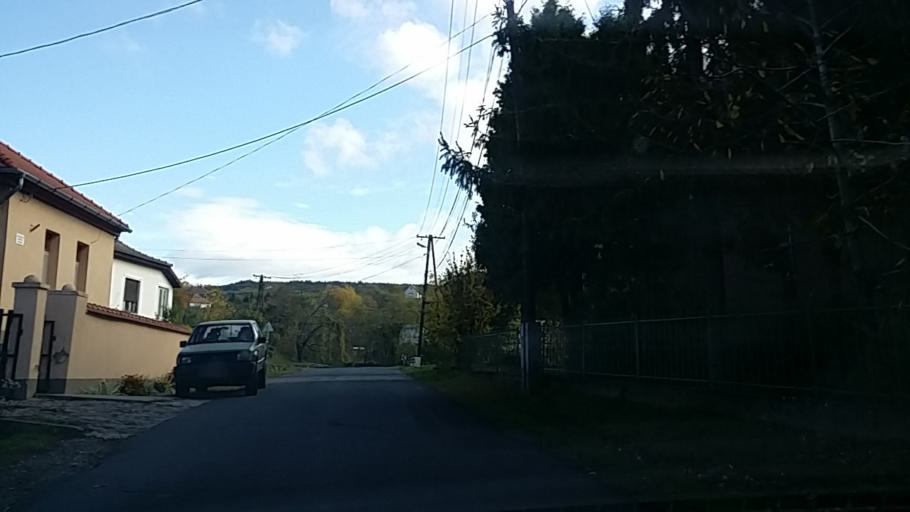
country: HU
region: Borsod-Abauj-Zemplen
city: Gonc
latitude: 48.3913
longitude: 21.2853
